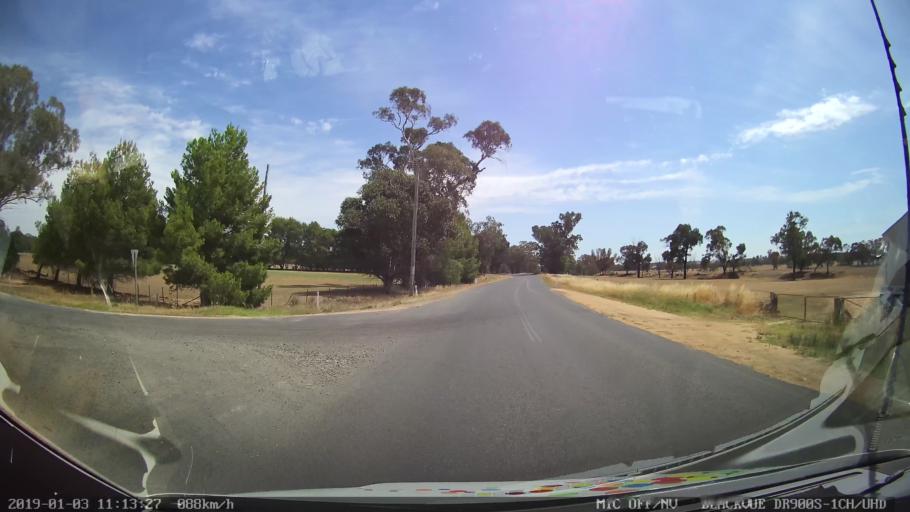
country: AU
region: New South Wales
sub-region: Young
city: Young
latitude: -34.1884
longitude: 148.2604
